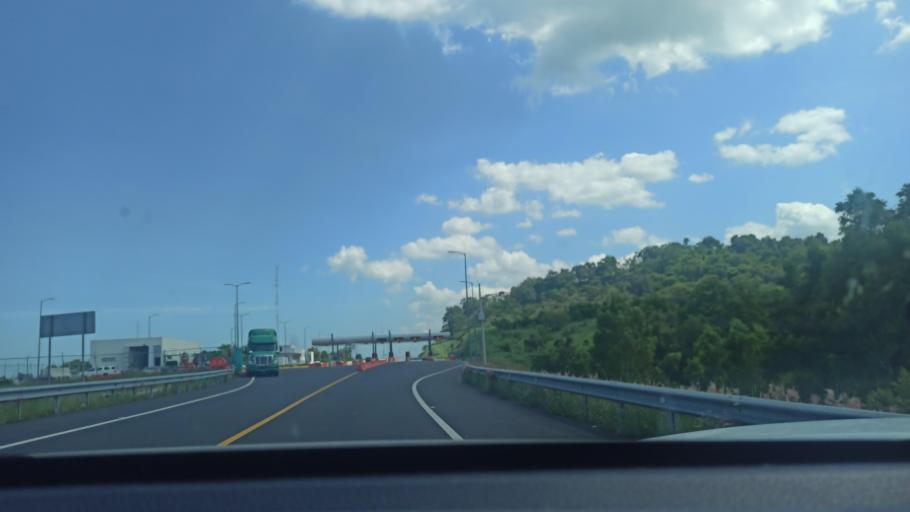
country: MX
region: Veracruz
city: Vega de Alatorre
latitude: 20.0455
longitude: -96.6859
